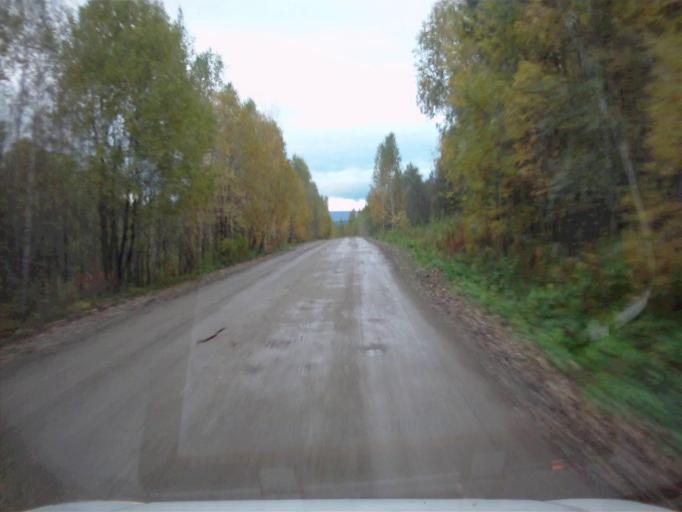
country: RU
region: Sverdlovsk
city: Mikhaylovsk
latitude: 56.1938
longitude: 59.1956
